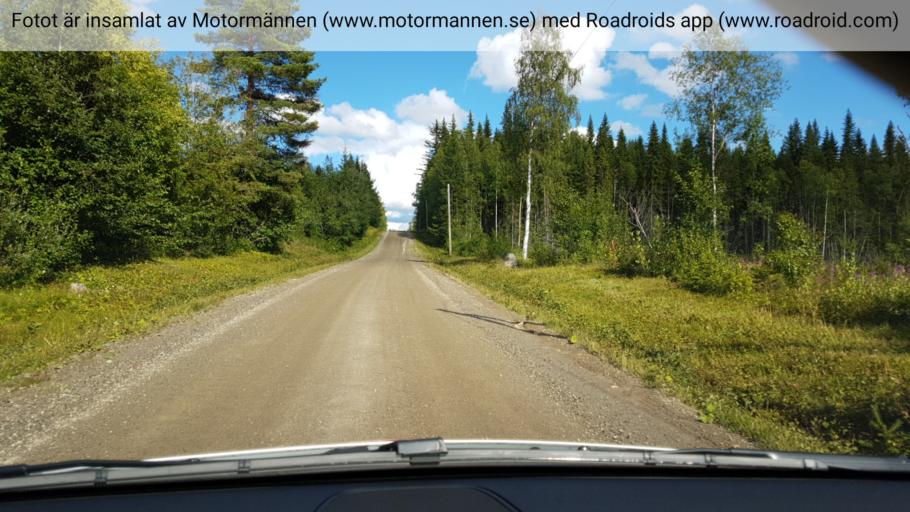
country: SE
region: Jaemtland
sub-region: Ragunda Kommun
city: Hammarstrand
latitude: 63.2776
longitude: 15.9314
